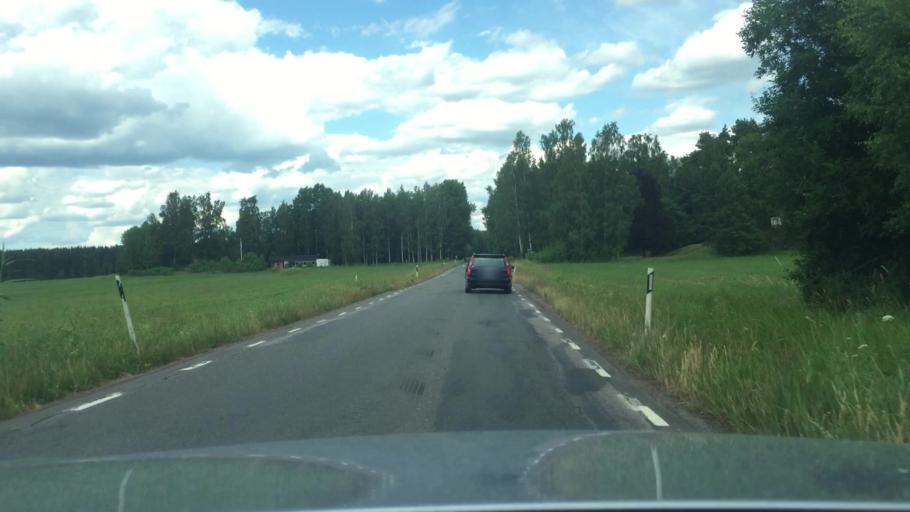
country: SE
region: Vaestra Goetaland
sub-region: Tidaholms Kommun
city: Tidaholm
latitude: 58.1960
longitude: 13.9783
